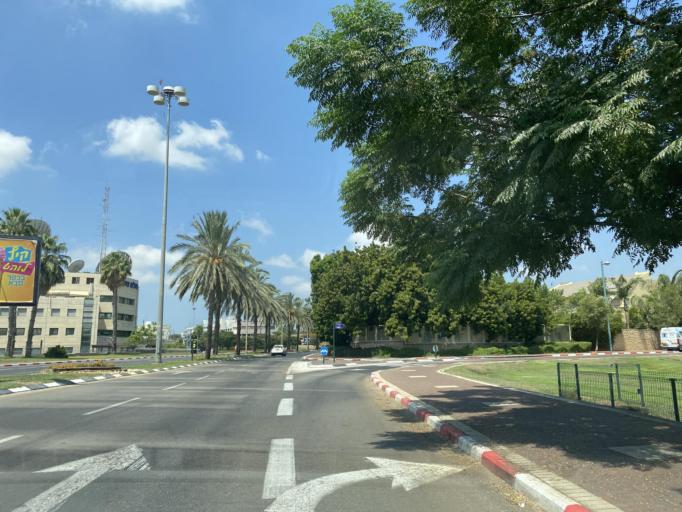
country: IL
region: Central District
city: Kfar Saba
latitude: 32.1776
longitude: 34.9314
